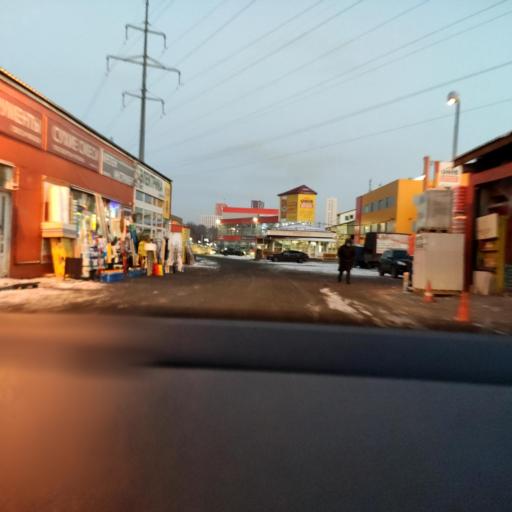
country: RU
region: Moskovskaya
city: Reutov
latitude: 55.7767
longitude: 37.8542
